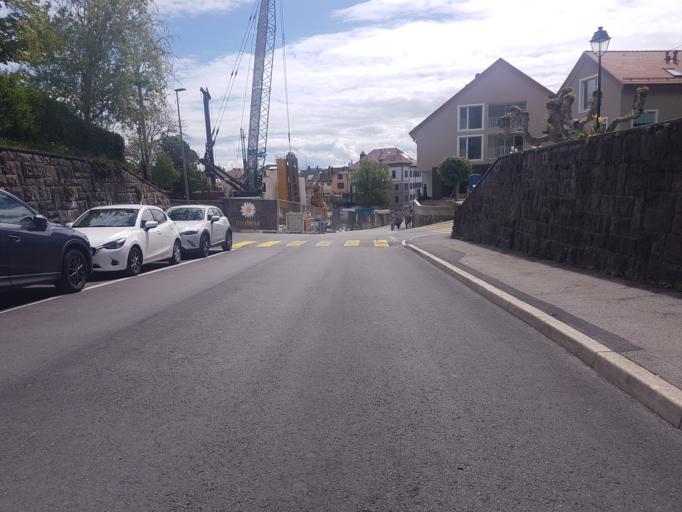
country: CH
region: Vaud
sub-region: Nyon District
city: Rolle
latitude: 46.4587
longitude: 6.3362
